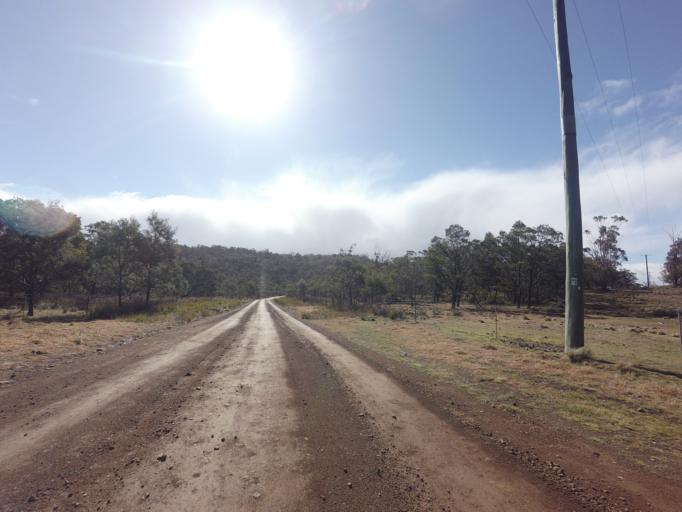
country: AU
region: Tasmania
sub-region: Sorell
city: Sorell
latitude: -42.4079
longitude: 147.9551
